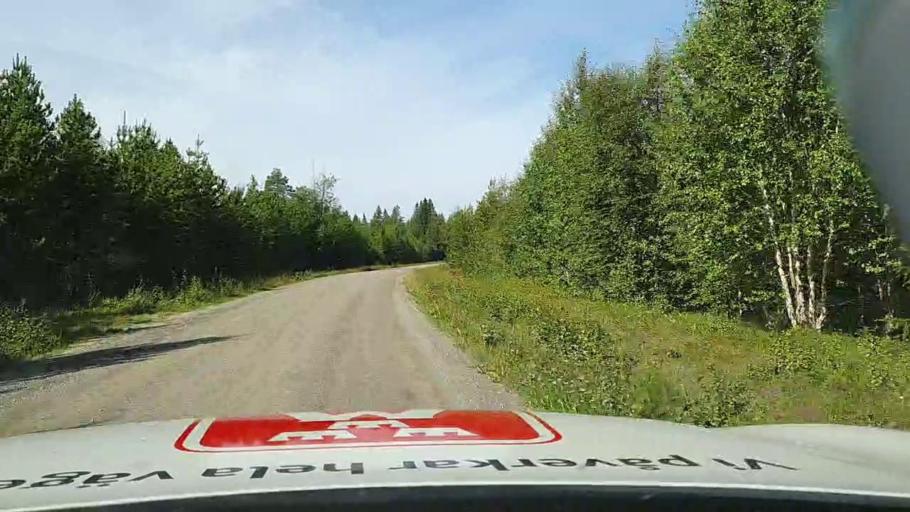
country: SE
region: Jaemtland
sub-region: Stroemsunds Kommun
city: Stroemsund
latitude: 63.7246
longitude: 15.2623
